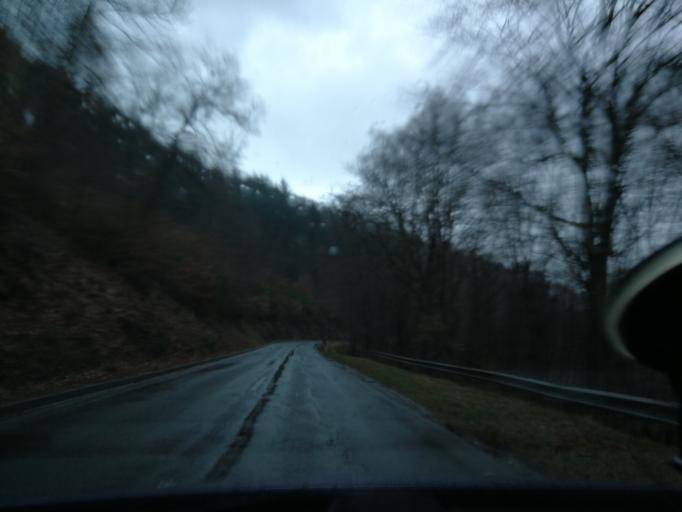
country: DE
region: Rheinland-Pfalz
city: Berglicht
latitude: 49.8016
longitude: 6.9560
